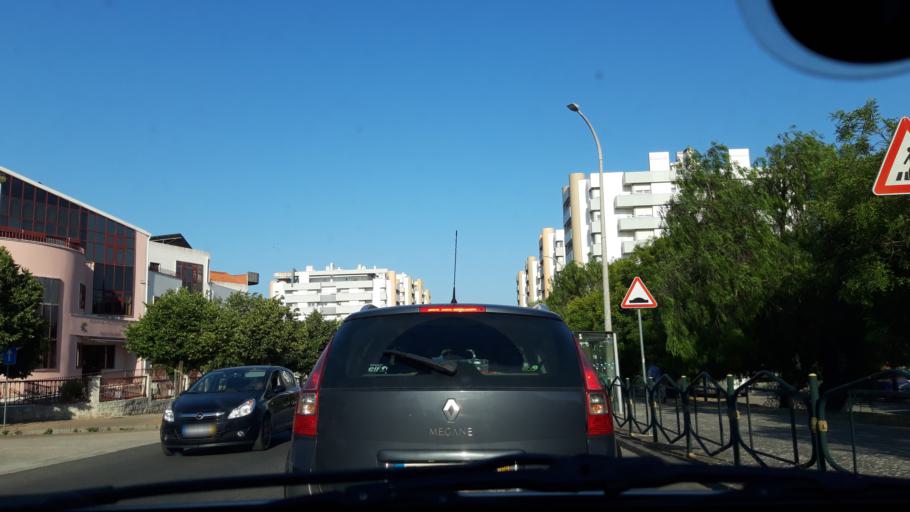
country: PT
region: Santarem
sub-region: Torres Novas
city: Torres Novas
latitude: 39.4739
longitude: -8.5456
